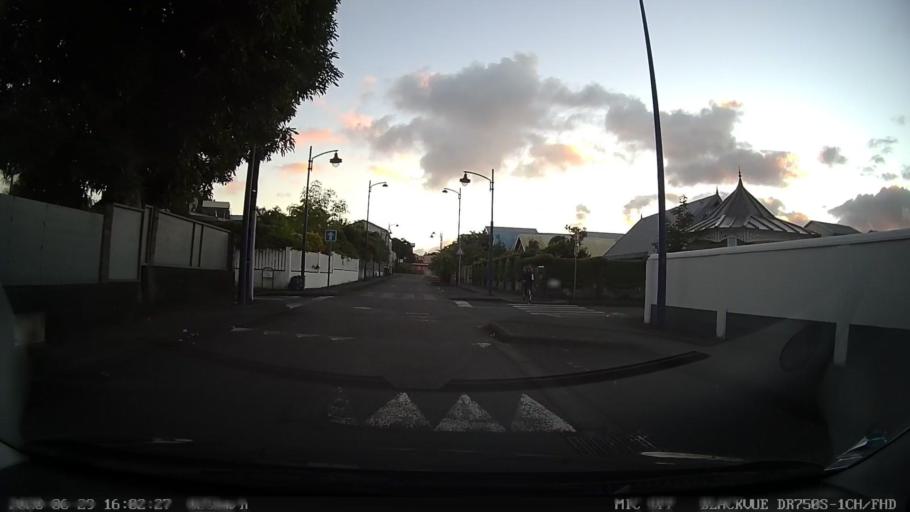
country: RE
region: Reunion
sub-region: Reunion
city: Bras-Panon
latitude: -20.9943
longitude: 55.6775
